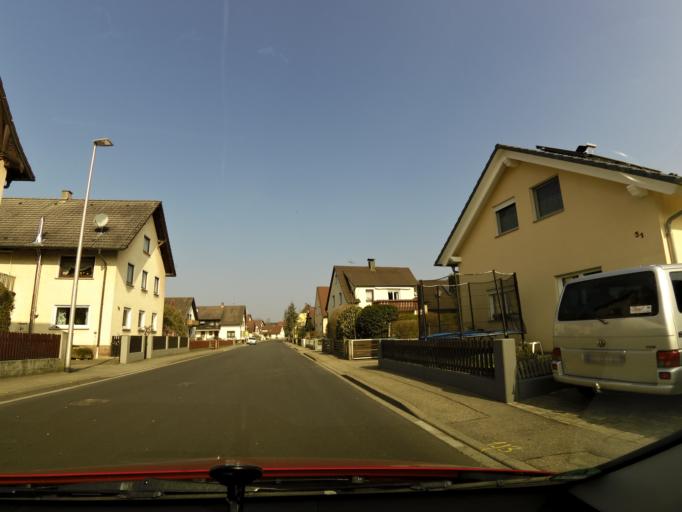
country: DE
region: Baden-Wuerttemberg
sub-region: Freiburg Region
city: Rheinau
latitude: 48.6208
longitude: 7.8925
